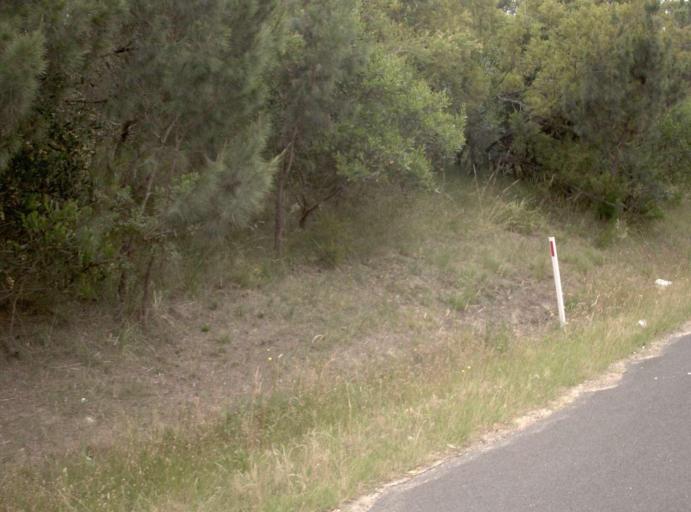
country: AU
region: Victoria
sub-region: Mornington Peninsula
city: Mount Martha
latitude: -38.2904
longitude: 145.0291
